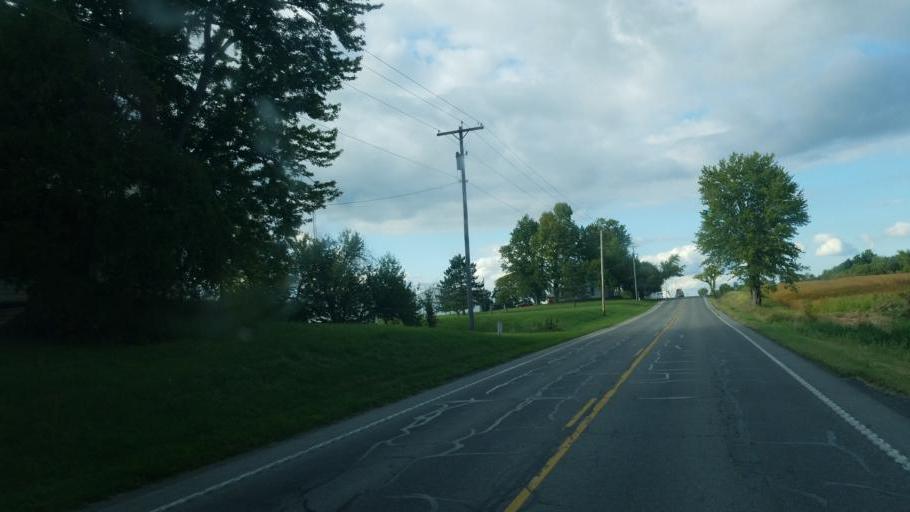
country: US
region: Ohio
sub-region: Huron County
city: Greenwich
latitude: 40.9184
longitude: -82.4985
